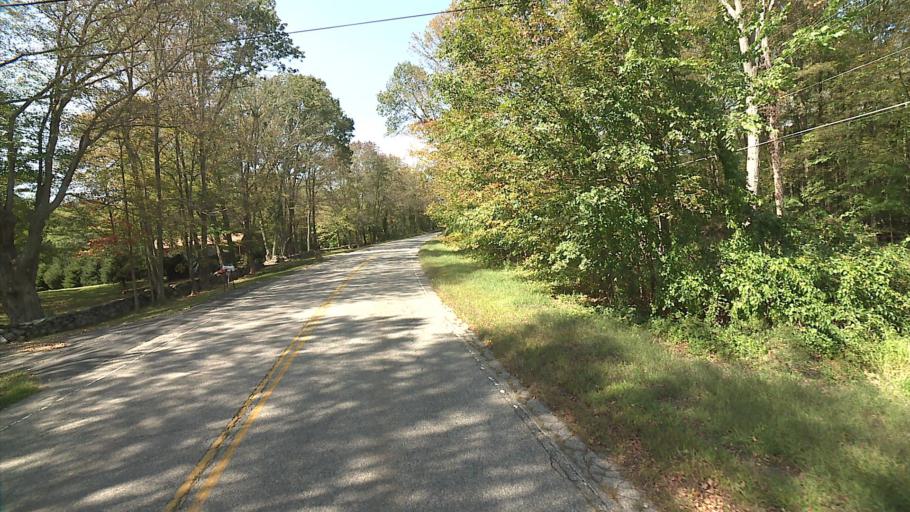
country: US
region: Connecticut
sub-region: Windham County
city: Willimantic
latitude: 41.6517
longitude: -72.2438
